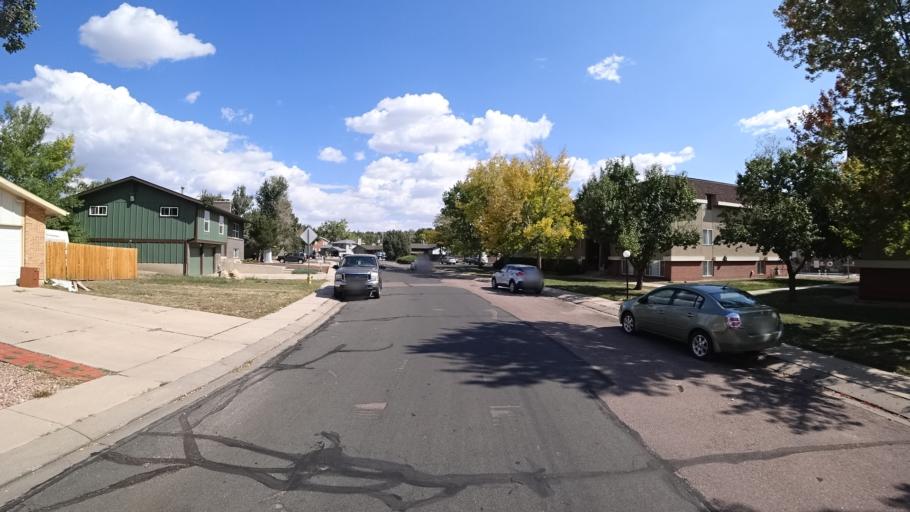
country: US
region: Colorado
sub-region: El Paso County
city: Cimarron Hills
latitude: 38.8706
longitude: -104.7548
